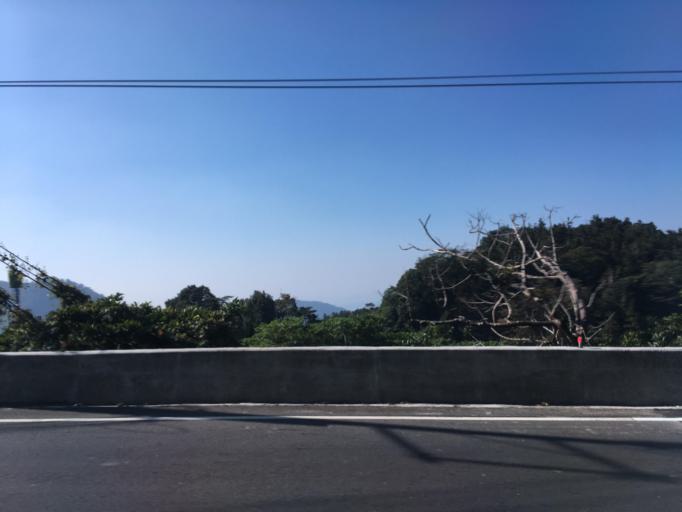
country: TW
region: Taiwan
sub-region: Chiayi
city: Jiayi Shi
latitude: 23.4152
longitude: 120.6447
